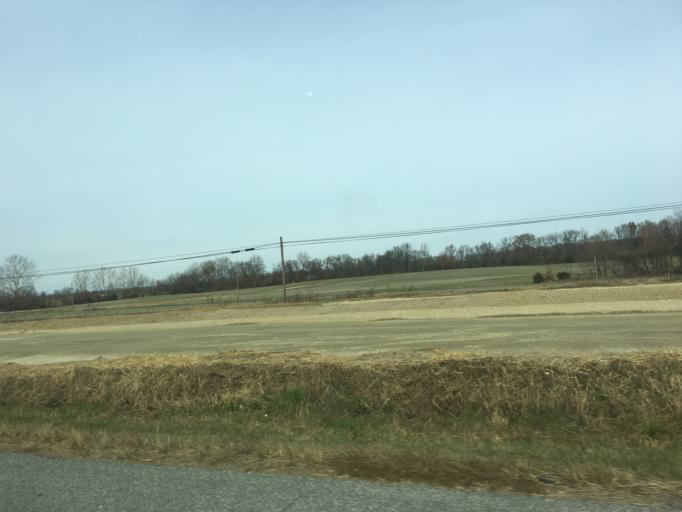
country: US
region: Maryland
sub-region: Queen Anne's County
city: Centreville
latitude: 38.9335
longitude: -76.0308
